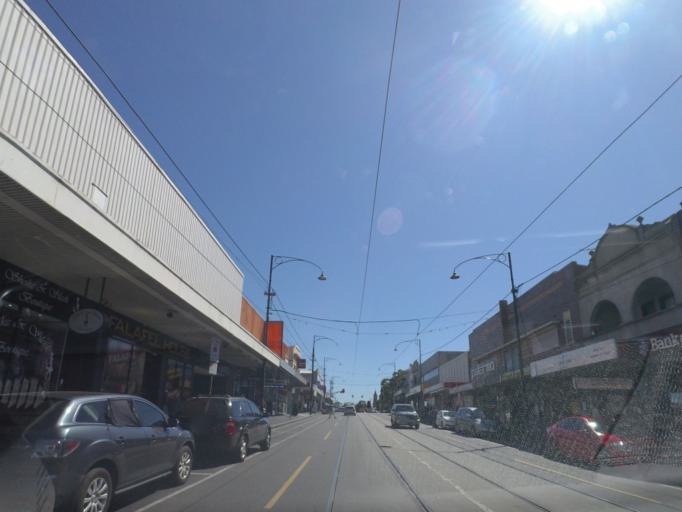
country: AU
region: Victoria
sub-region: Moreland
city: Coburg
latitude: -37.7425
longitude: 144.9663
